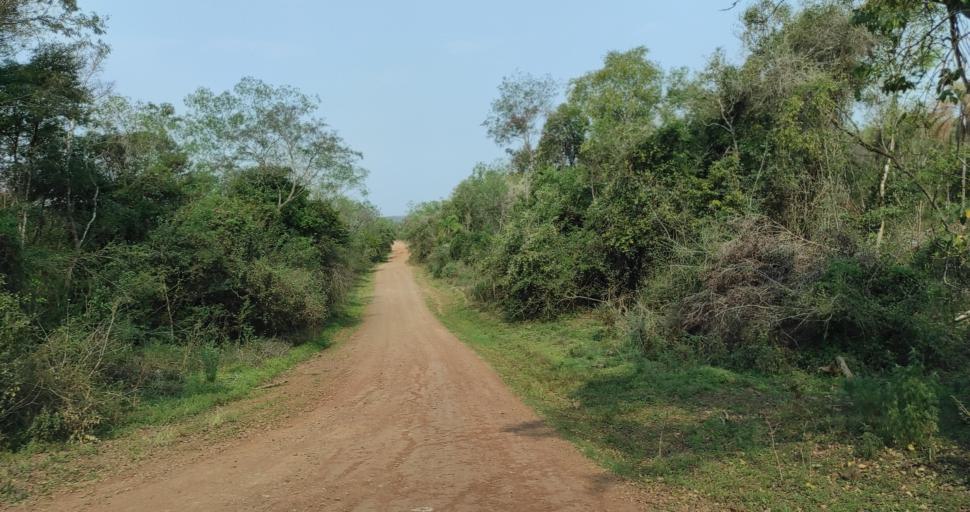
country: AR
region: Misiones
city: Cerro Cora
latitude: -27.5359
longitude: -55.5885
